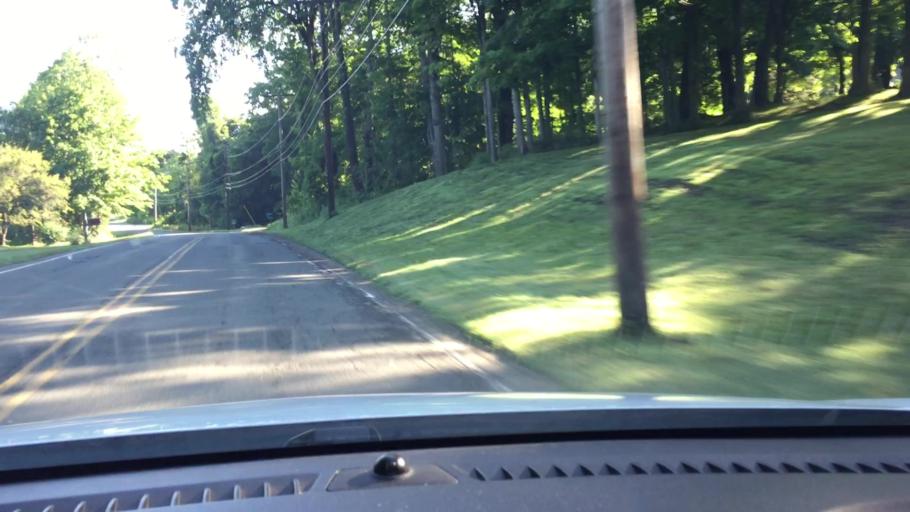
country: US
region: Massachusetts
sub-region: Berkshire County
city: Pittsfield
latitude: 42.4191
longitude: -73.2257
